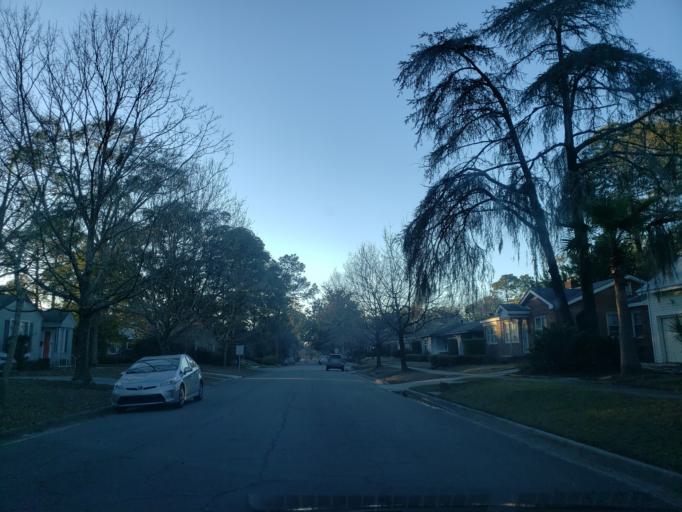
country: US
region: Georgia
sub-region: Chatham County
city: Thunderbolt
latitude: 32.0395
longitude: -81.0898
